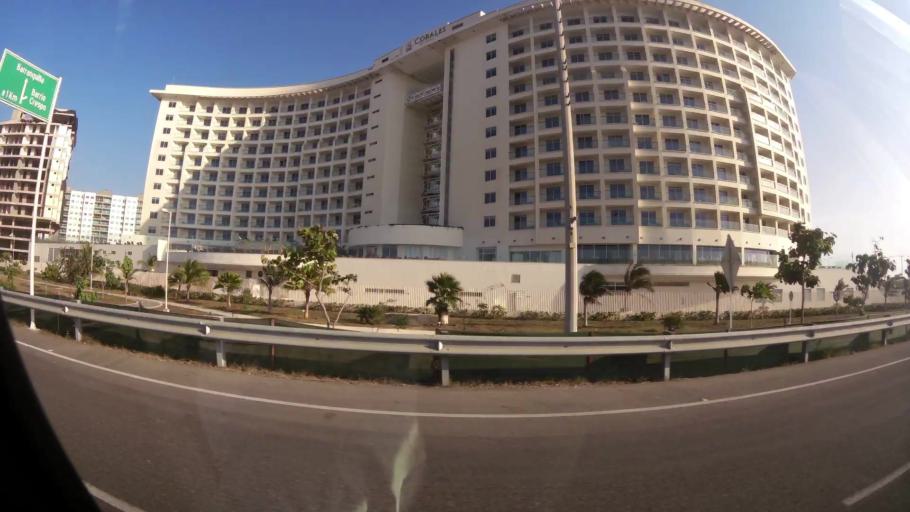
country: CO
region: Bolivar
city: Cartagena
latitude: 10.4435
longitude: -75.5259
